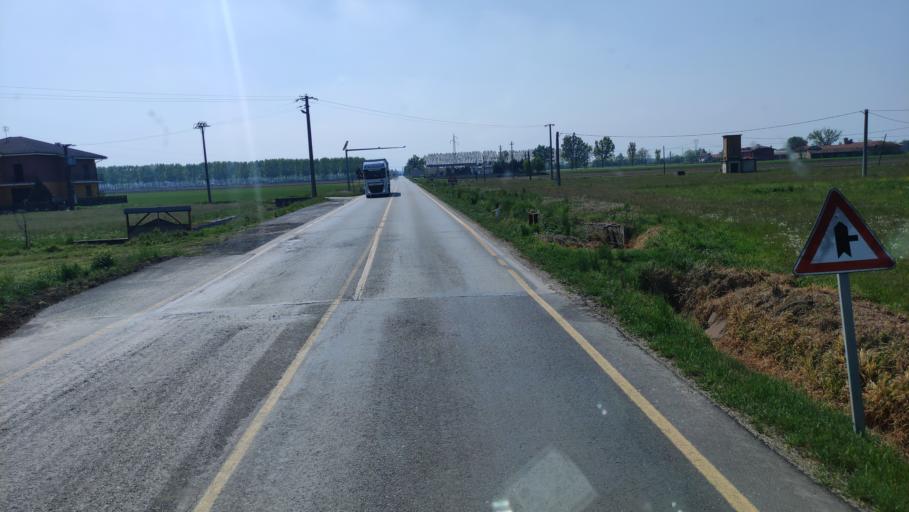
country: IT
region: Piedmont
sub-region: Provincia di Cuneo
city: Marene
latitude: 44.6562
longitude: 7.7126
